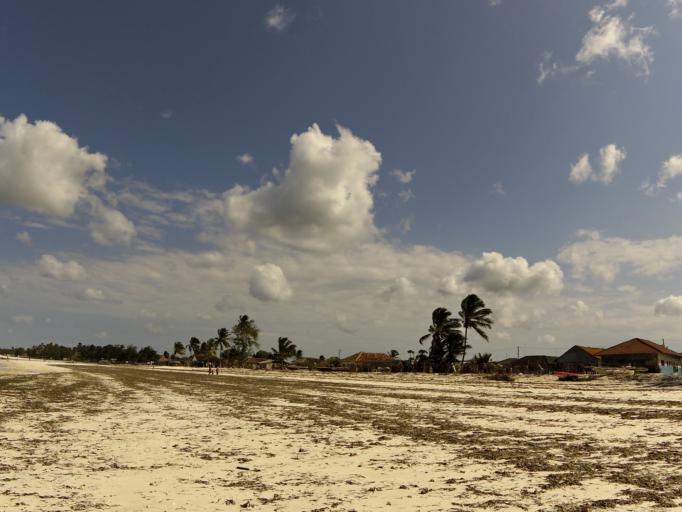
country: TZ
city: Kiwengwa
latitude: -6.0899
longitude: 39.4261
